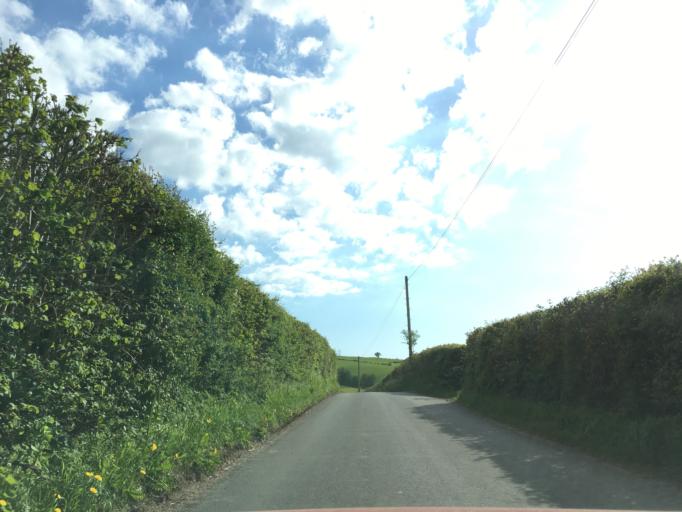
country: GB
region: Wales
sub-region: Newport
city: Marshfield
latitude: 51.5708
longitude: -3.0563
